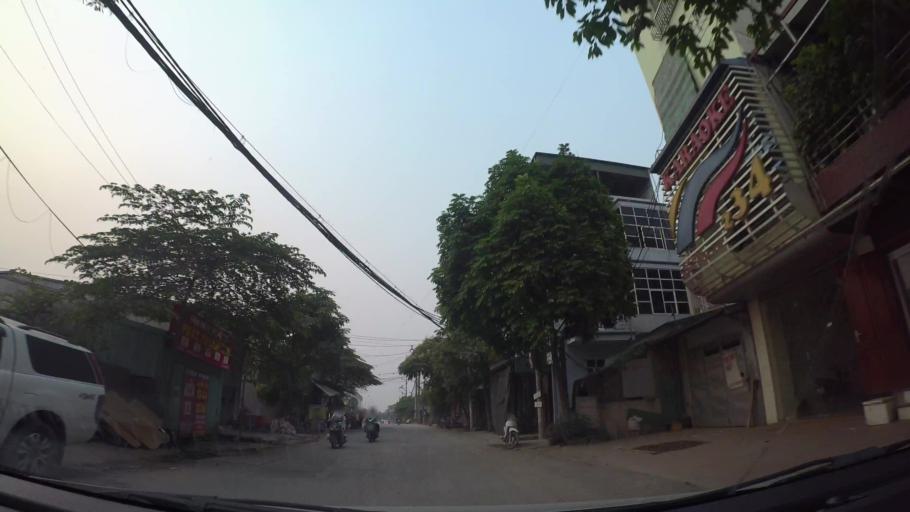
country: VN
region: Ha Noi
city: Ha Dong
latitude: 20.9962
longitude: 105.7246
